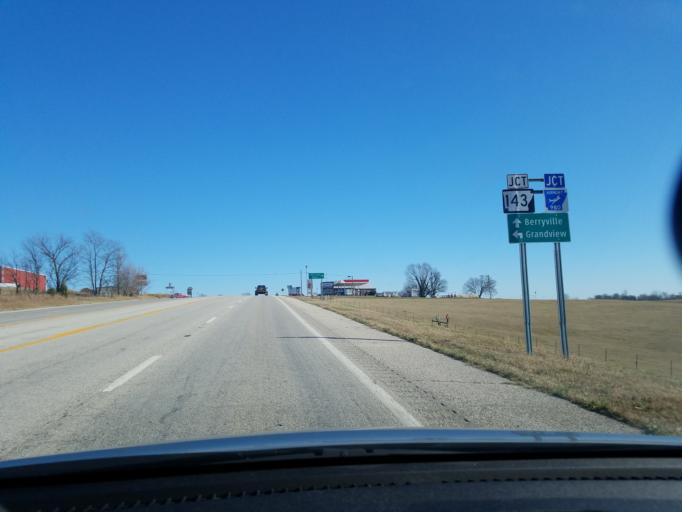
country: US
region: Arkansas
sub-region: Carroll County
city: Berryville
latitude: 36.3901
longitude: -93.6236
